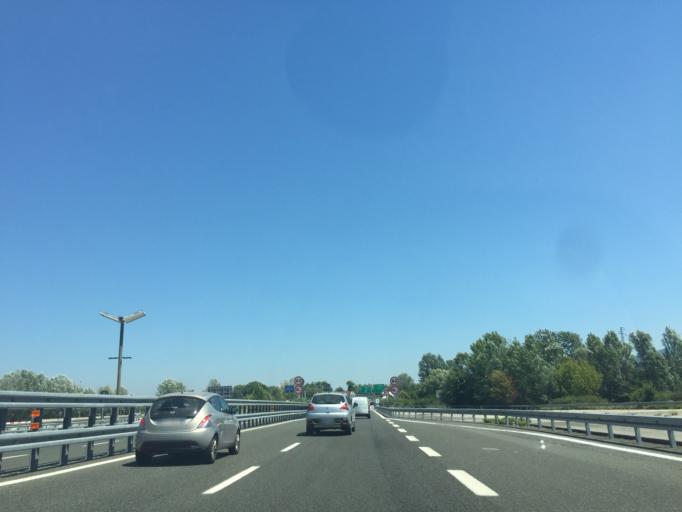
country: IT
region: Tuscany
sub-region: Provincia di Lucca
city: Lucca
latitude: 43.8366
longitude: 10.4692
